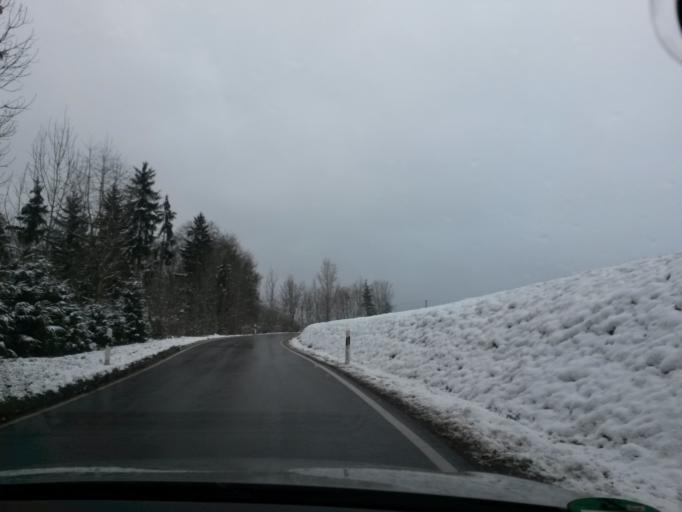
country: DE
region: Baden-Wuerttemberg
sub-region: Tuebingen Region
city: Amstetten
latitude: 48.5876
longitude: 9.8574
